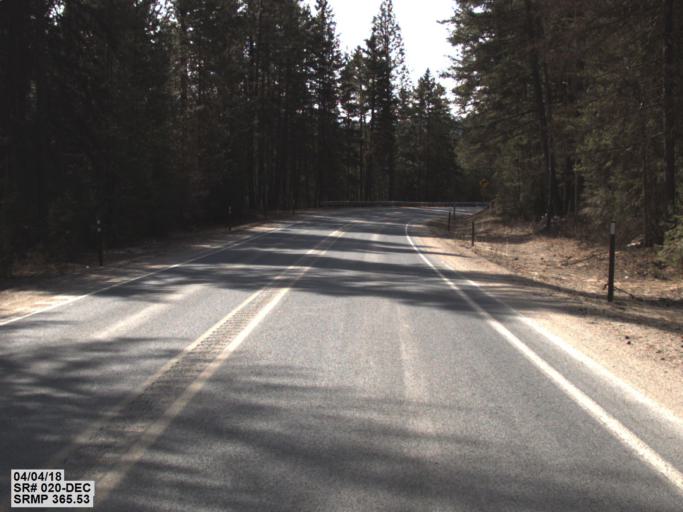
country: US
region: Washington
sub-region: Stevens County
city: Colville
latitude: 48.5064
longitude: -117.7079
